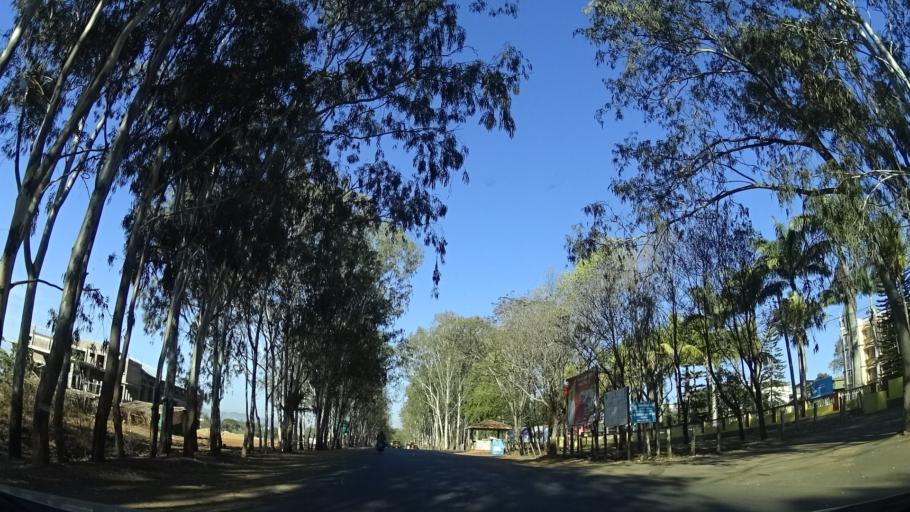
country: IN
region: Karnataka
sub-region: Chikmagalur
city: Chikmagalur
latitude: 13.3383
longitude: 75.8108
